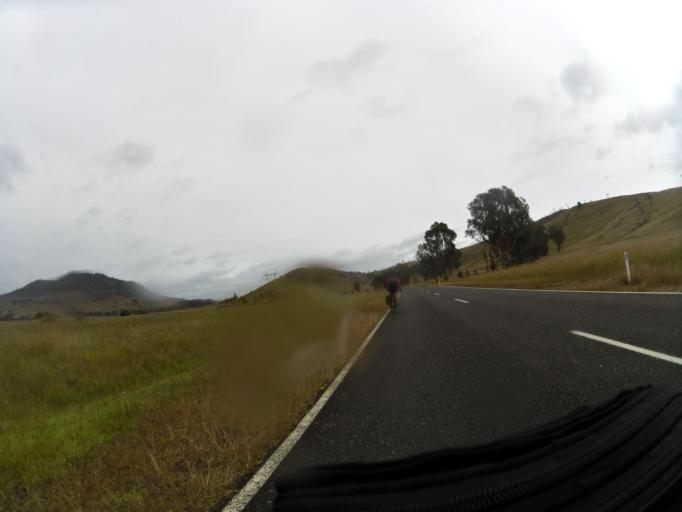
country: AU
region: New South Wales
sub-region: Greater Hume Shire
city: Holbrook
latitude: -36.2076
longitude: 147.7368
